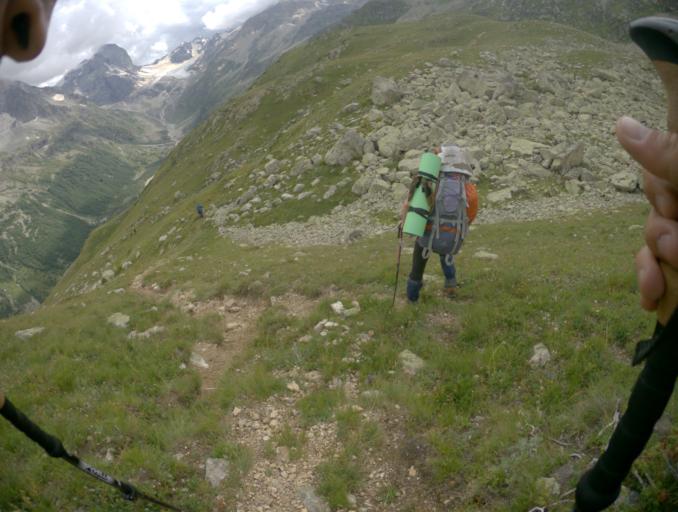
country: RU
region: Karachayevo-Cherkesiya
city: Uchkulan
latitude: 43.2686
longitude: 42.1284
